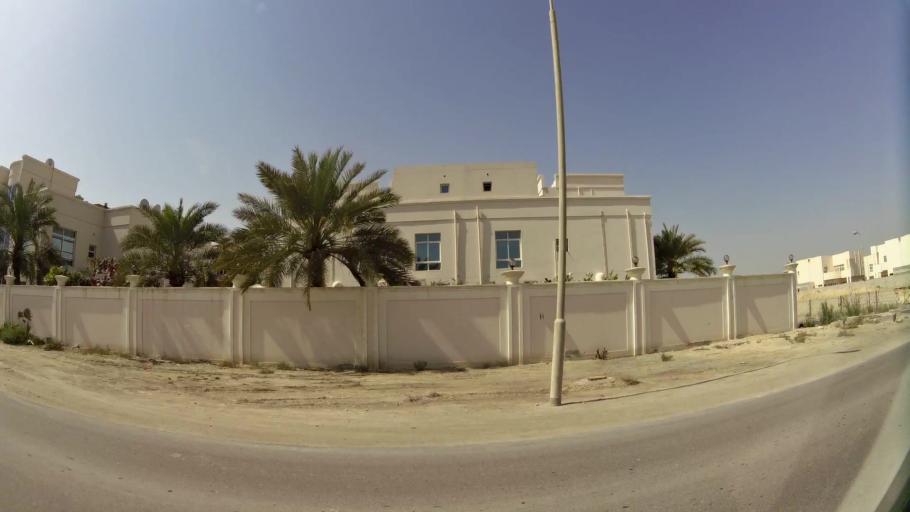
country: BH
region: Northern
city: Madinat `Isa
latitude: 26.1935
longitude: 50.4677
